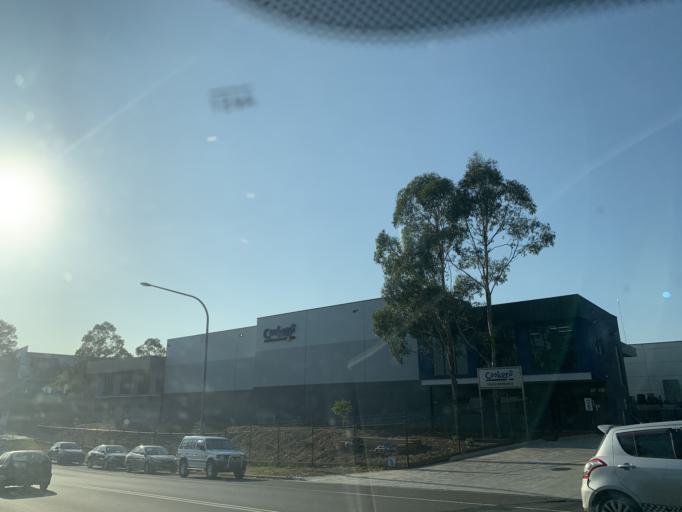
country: AU
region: New South Wales
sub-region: Blacktown
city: Doonside
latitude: -33.7973
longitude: 150.8768
